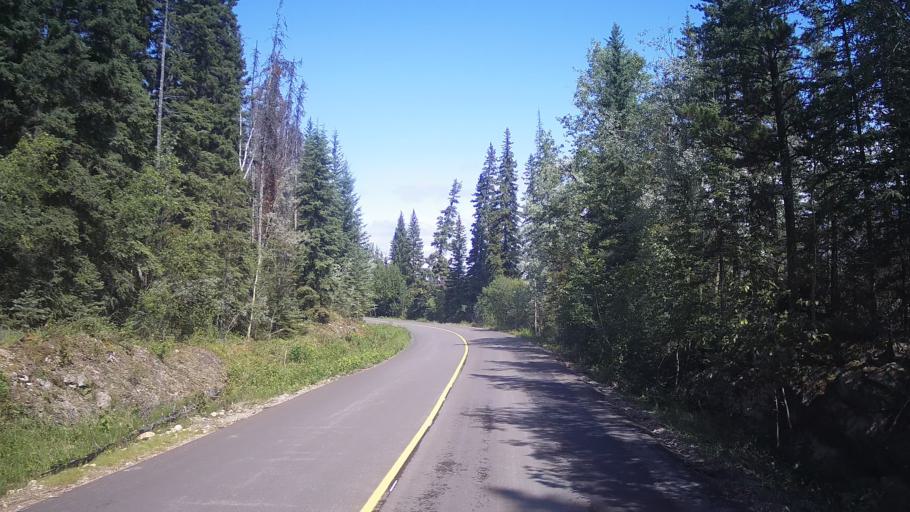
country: CA
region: Alberta
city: Jasper Park Lodge
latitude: 52.7378
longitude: -117.9579
